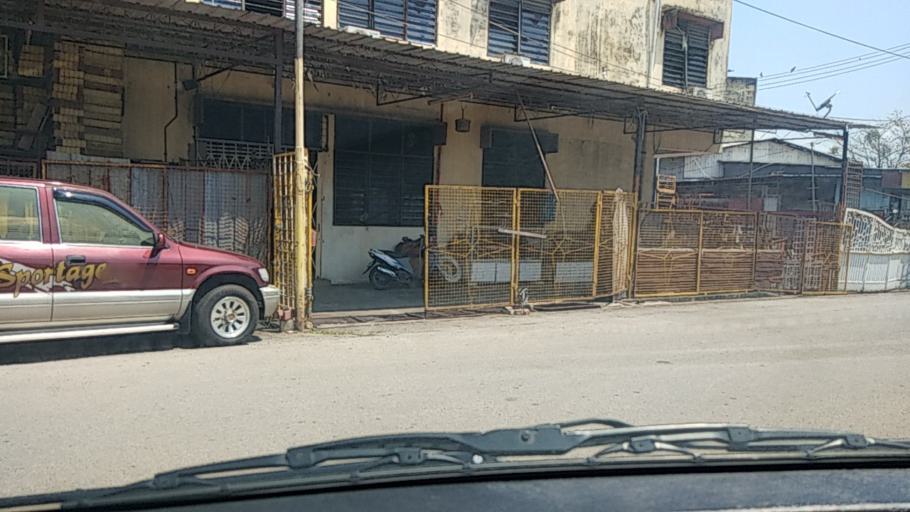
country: MY
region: Kedah
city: Sungai Petani
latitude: 5.6356
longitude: 100.4979
